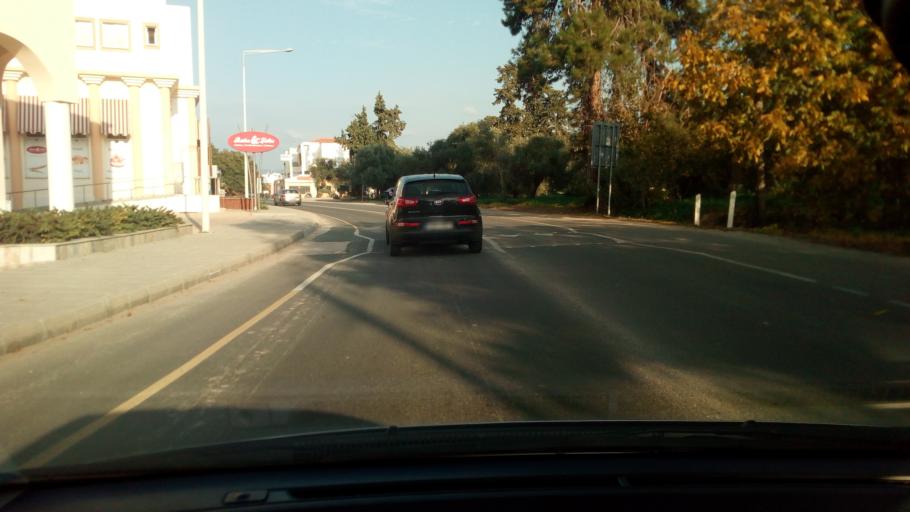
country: CY
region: Pafos
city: Polis
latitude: 35.0292
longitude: 32.4189
